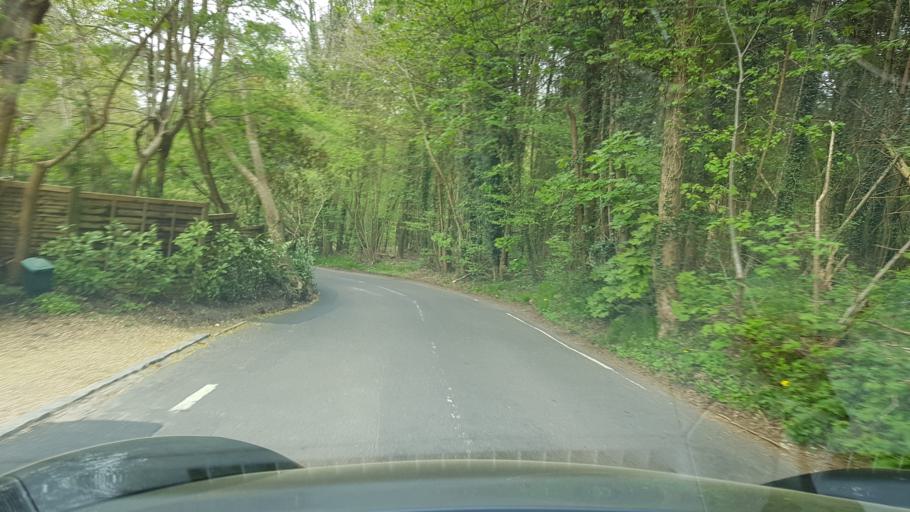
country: GB
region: England
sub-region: Surrey
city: East Horsley
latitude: 51.2526
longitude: -0.4270
